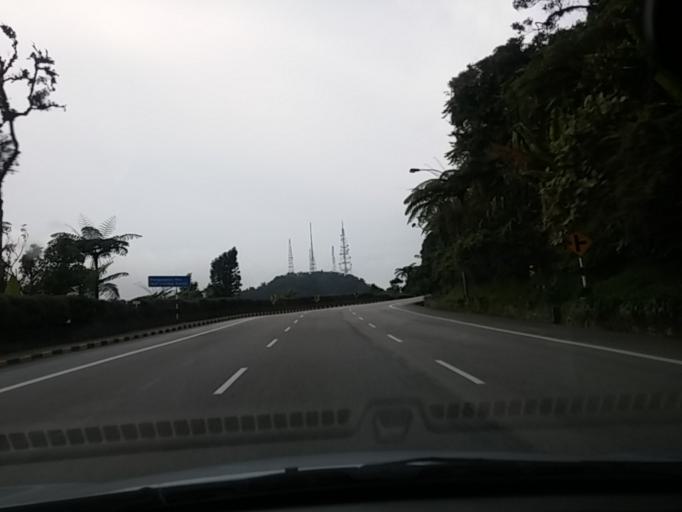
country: MY
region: Pahang
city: Kampung Bukit Tinggi, Bentong
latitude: 3.4201
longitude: 101.7893
